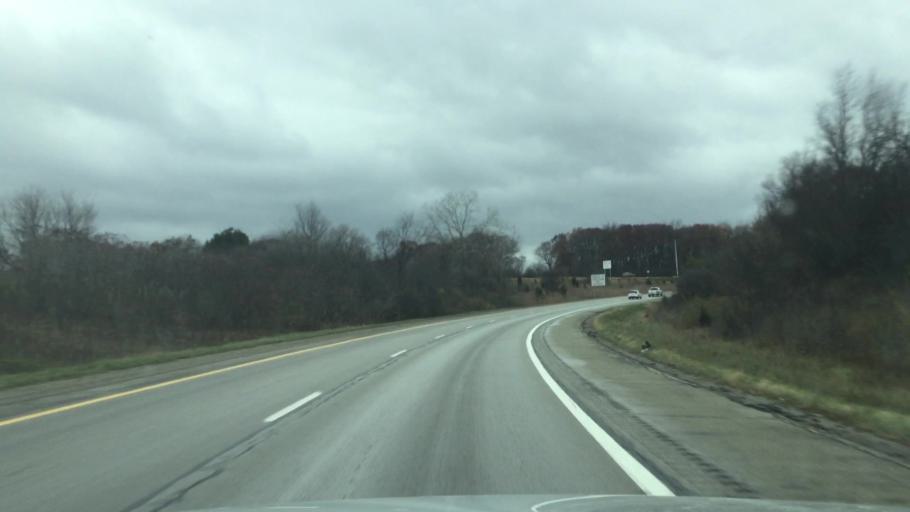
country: US
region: Michigan
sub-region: Washtenaw County
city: Ann Arbor
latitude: 42.3219
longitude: -83.7380
